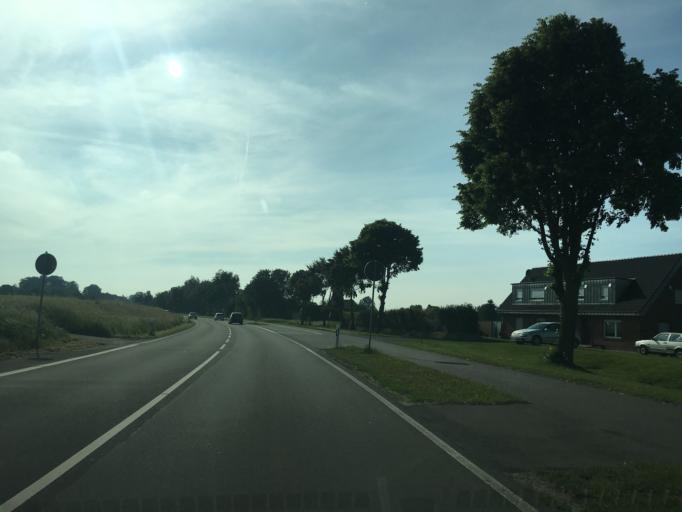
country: DE
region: North Rhine-Westphalia
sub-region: Regierungsbezirk Munster
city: Greven
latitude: 52.0965
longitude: 7.5764
